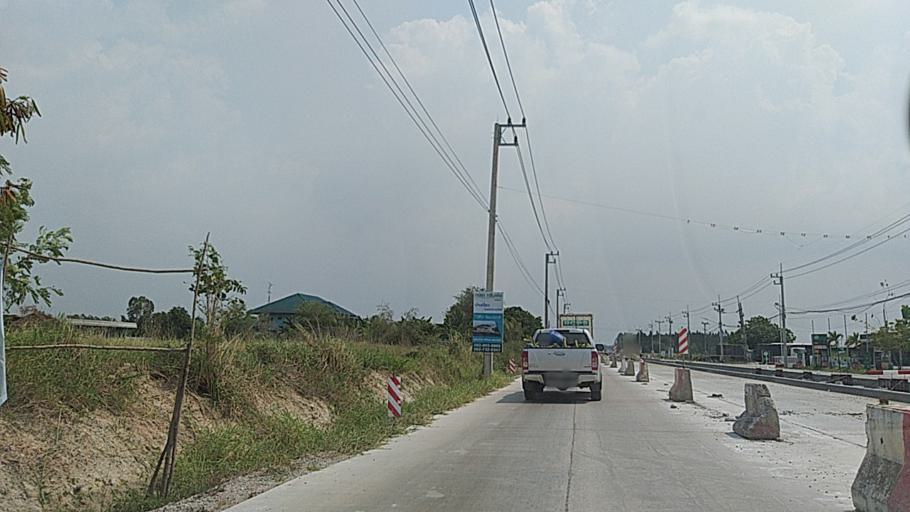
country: TH
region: Chon Buri
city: Phanat Nikhom
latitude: 13.3813
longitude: 101.1938
